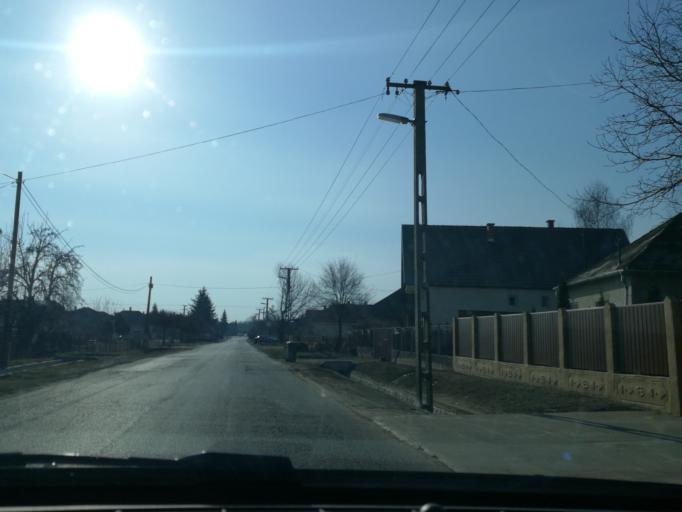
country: HU
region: Szabolcs-Szatmar-Bereg
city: Levelek
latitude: 47.9702
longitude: 21.9814
